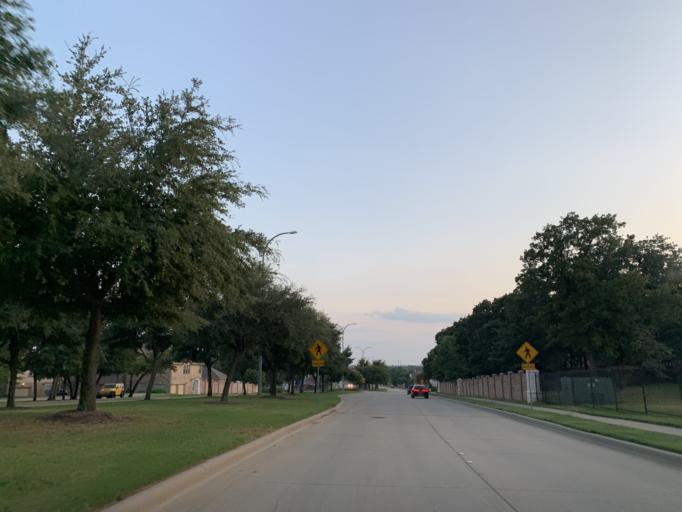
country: US
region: Texas
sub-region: Tarrant County
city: Keller
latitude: 32.9506
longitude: -97.2655
